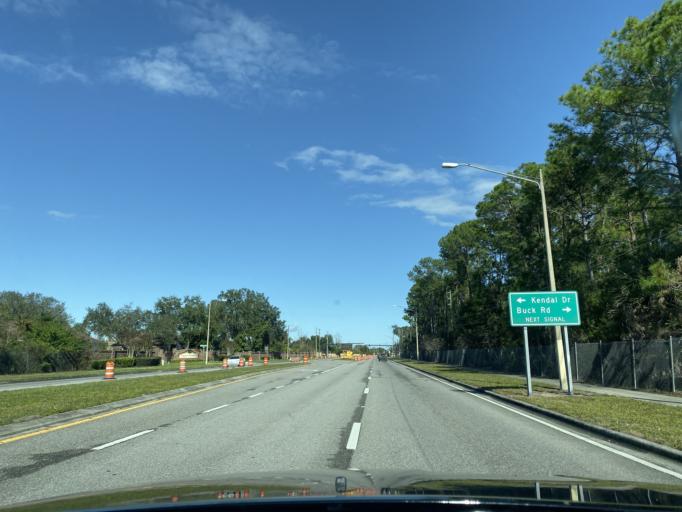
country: US
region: Florida
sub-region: Orange County
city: Alafaya
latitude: 28.5875
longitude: -81.2450
